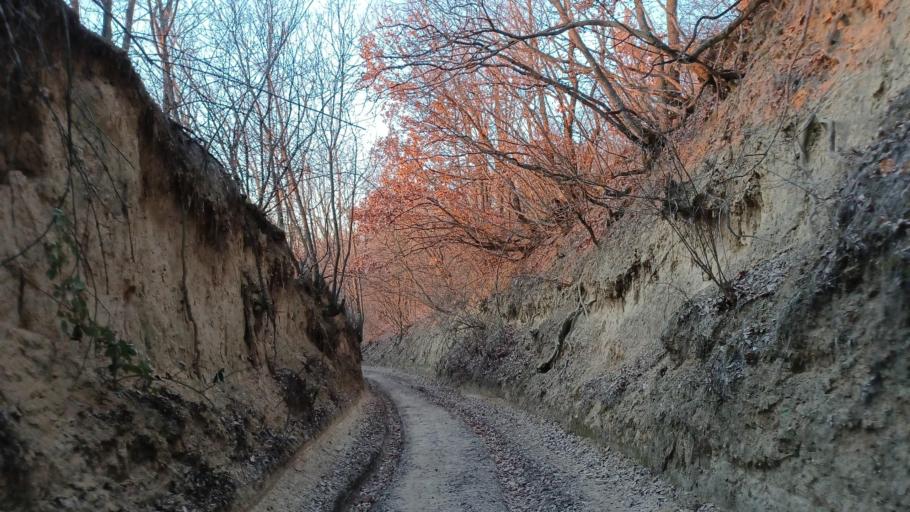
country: HU
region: Tolna
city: Szentgalpuszta
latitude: 46.3402
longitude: 18.6448
